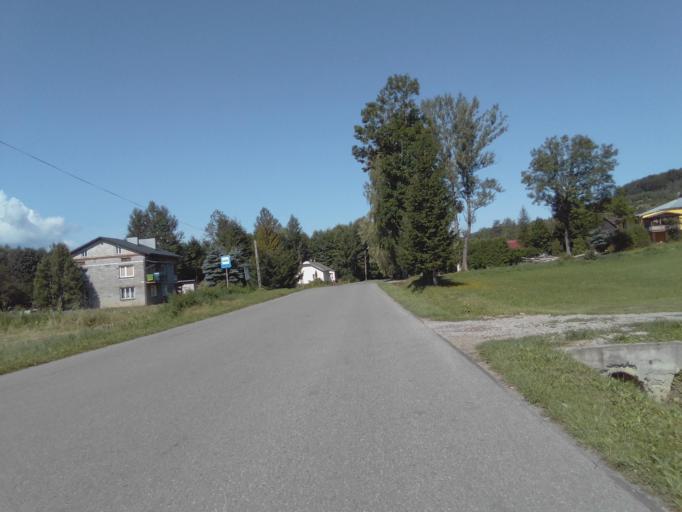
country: PL
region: Subcarpathian Voivodeship
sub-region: Powiat krosnienski
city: Chorkowka
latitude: 49.6108
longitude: 21.6211
